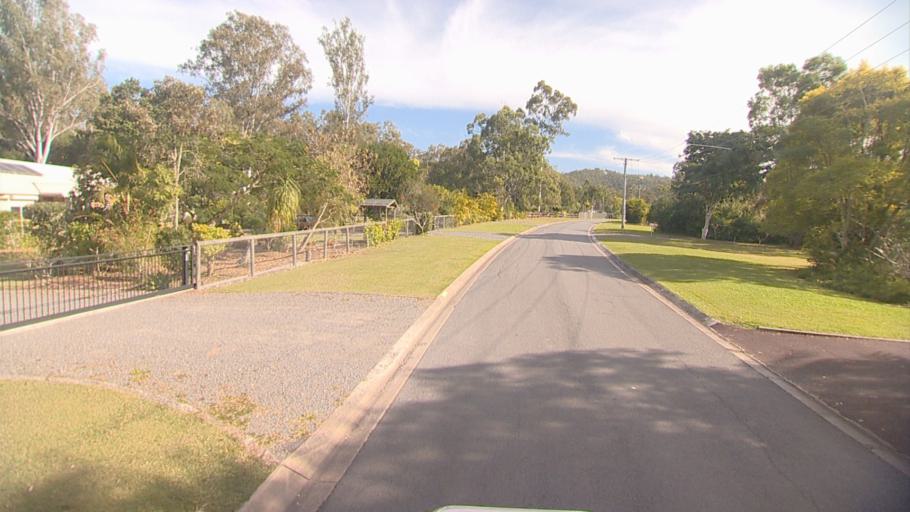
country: AU
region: Queensland
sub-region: Logan
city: Windaroo
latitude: -27.7628
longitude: 153.1957
